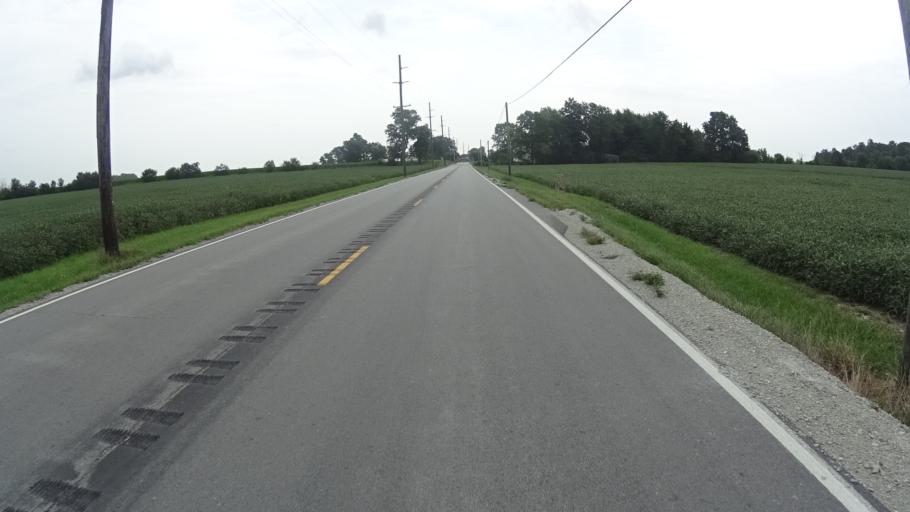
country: US
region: Indiana
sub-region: Madison County
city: Lapel
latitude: 40.0176
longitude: -85.8317
